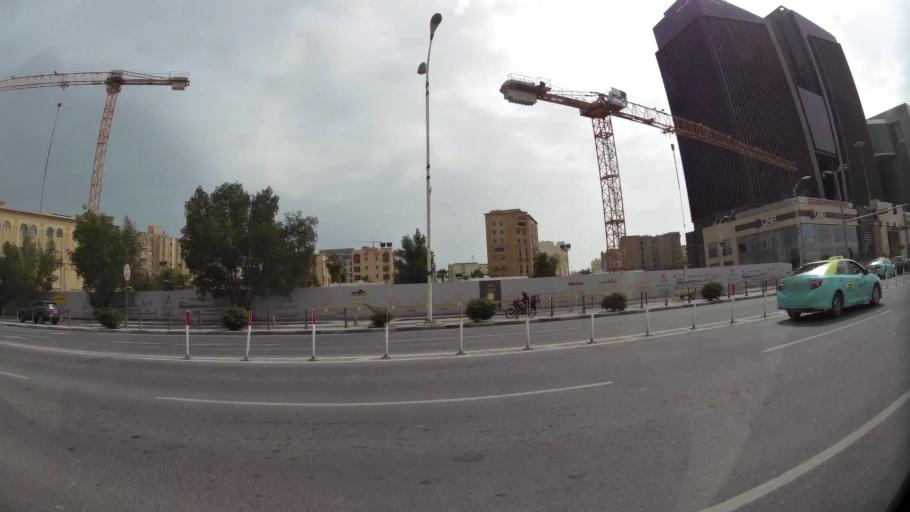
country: QA
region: Baladiyat ad Dawhah
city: Doha
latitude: 25.2821
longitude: 51.5064
